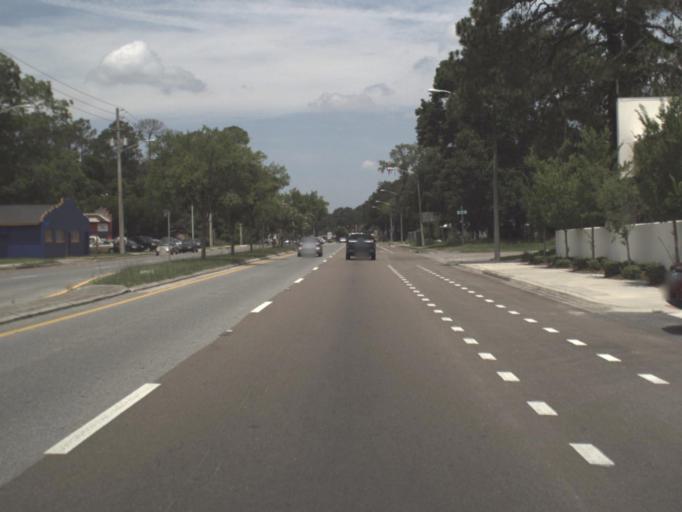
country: US
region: Florida
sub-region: Alachua County
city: Gainesville
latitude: 29.6496
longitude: -82.3025
